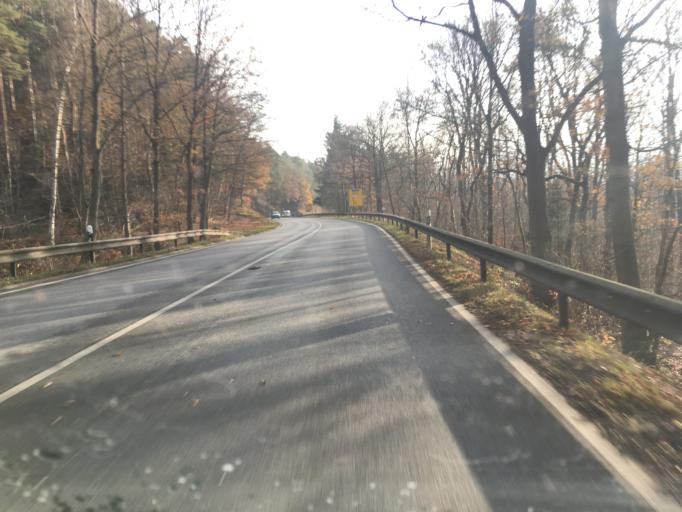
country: DE
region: North Rhine-Westphalia
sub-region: Regierungsbezirk Koln
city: Kall
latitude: 50.5583
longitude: 6.5405
